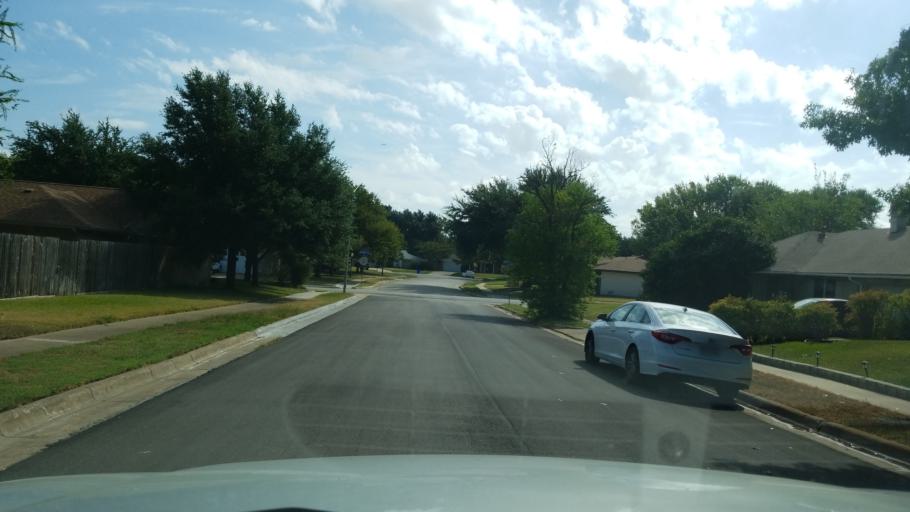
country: US
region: Texas
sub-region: Tarrant County
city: Euless
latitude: 32.8430
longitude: -97.0791
